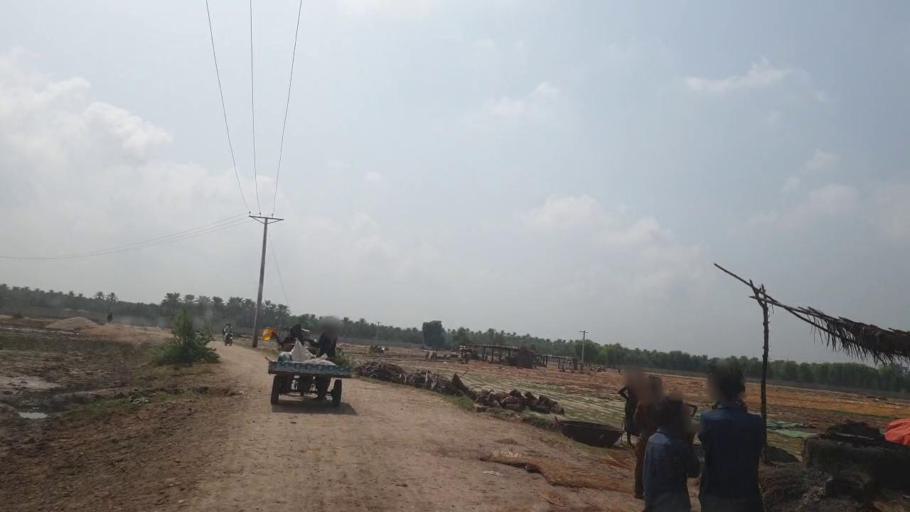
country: PK
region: Sindh
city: Khairpur
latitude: 27.5110
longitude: 68.7453
